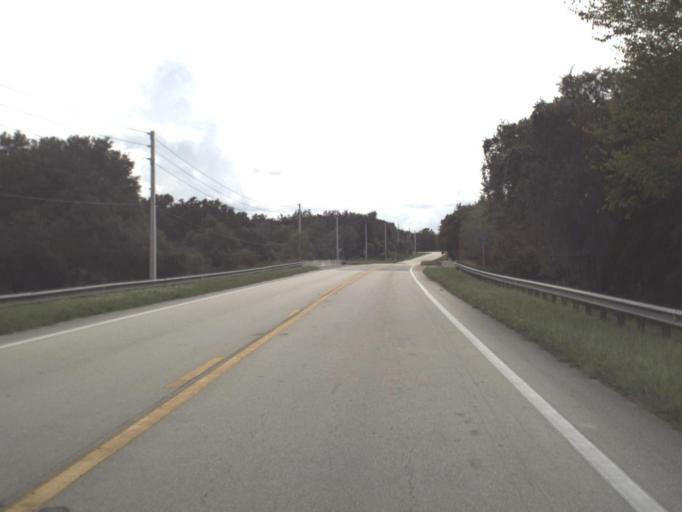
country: US
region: Florida
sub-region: DeSoto County
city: Southeast Arcadia
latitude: 27.1796
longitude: -81.8279
